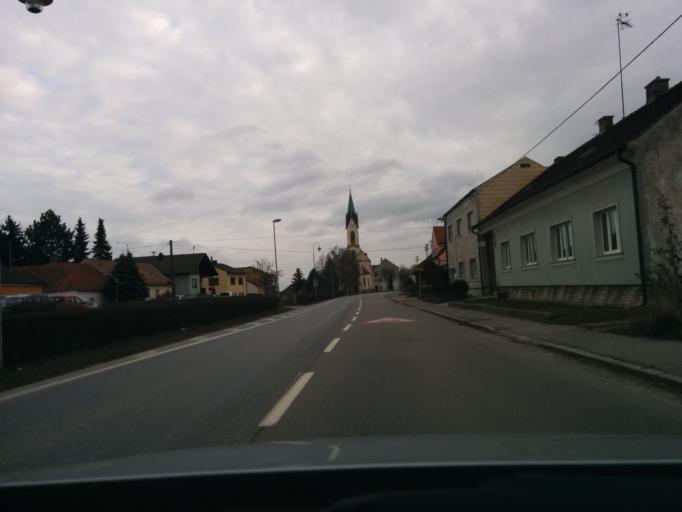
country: AT
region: Lower Austria
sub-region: Politischer Bezirk Mistelbach
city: Asparn an der Zaya
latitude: 48.6087
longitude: 16.5400
